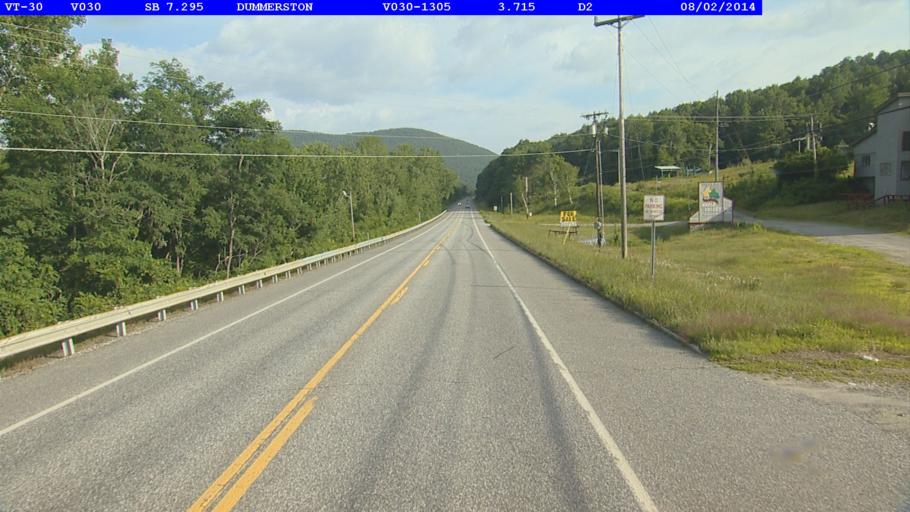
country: US
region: Vermont
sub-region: Windham County
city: Newfane
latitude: 42.9454
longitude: -72.6176
